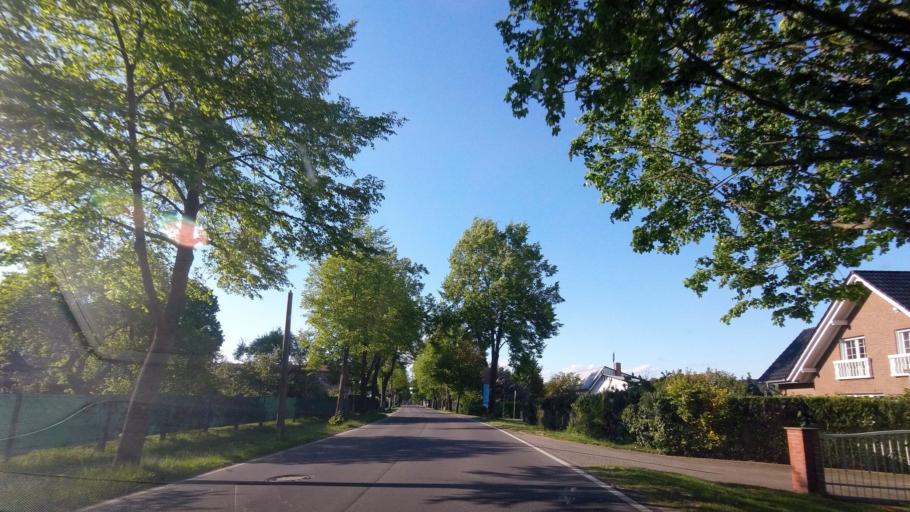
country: DE
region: Brandenburg
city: Luebben
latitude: 51.9269
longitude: 13.8957
